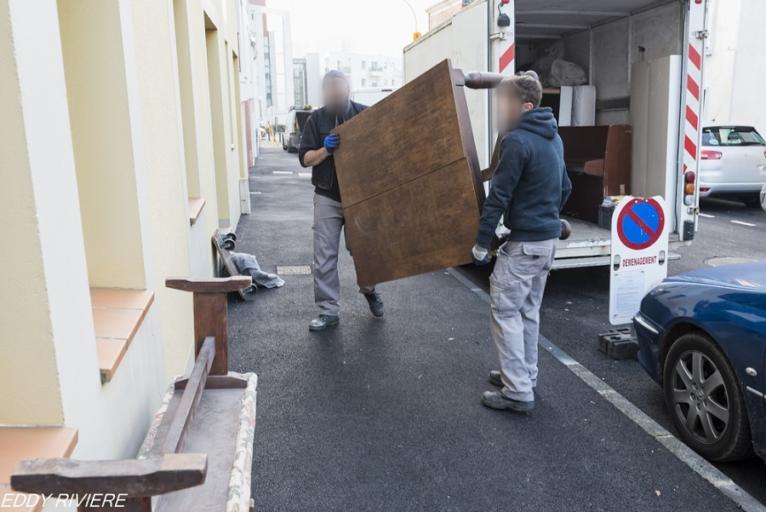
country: FR
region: Pays de la Loire
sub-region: Departement de la Loire-Atlantique
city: Bouguenais
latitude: 47.2011
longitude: -1.6272
